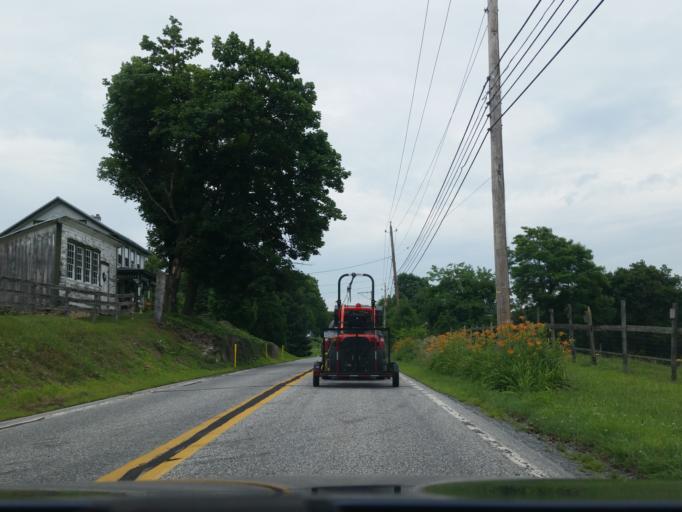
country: US
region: Pennsylvania
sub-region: Lebanon County
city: Palmyra
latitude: 40.3931
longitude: -76.6073
